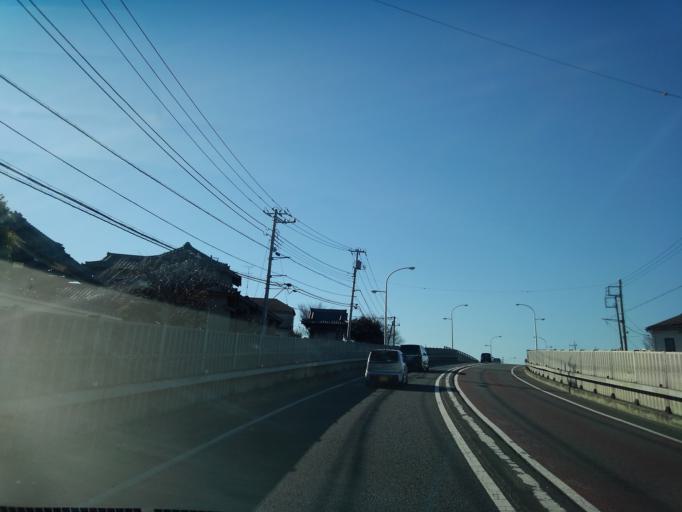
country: JP
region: Tokyo
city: Hino
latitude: 35.6847
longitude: 139.3704
